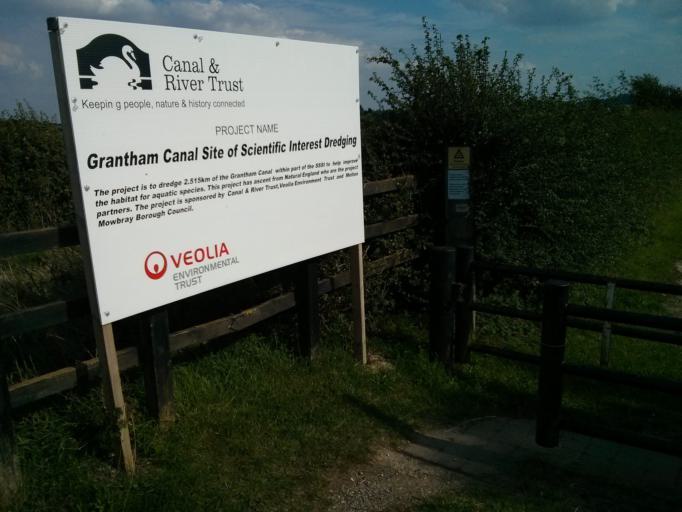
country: GB
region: England
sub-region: Lincolnshire
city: Long Bennington
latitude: 52.9144
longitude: -0.8269
